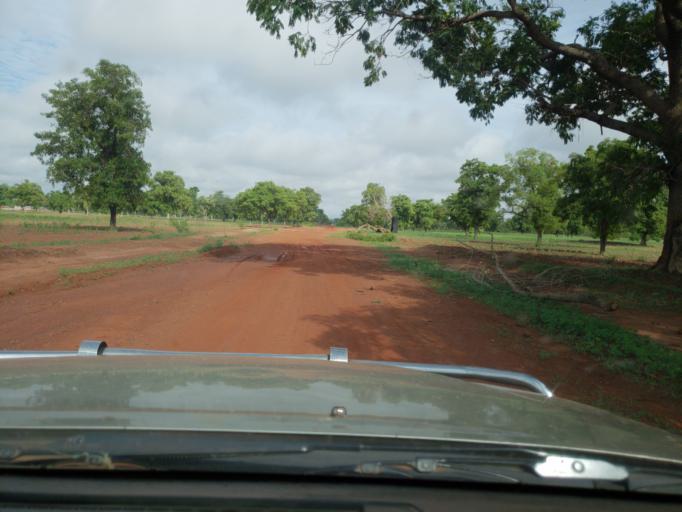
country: ML
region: Sikasso
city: Koutiala
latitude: 12.3925
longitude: -6.0116
